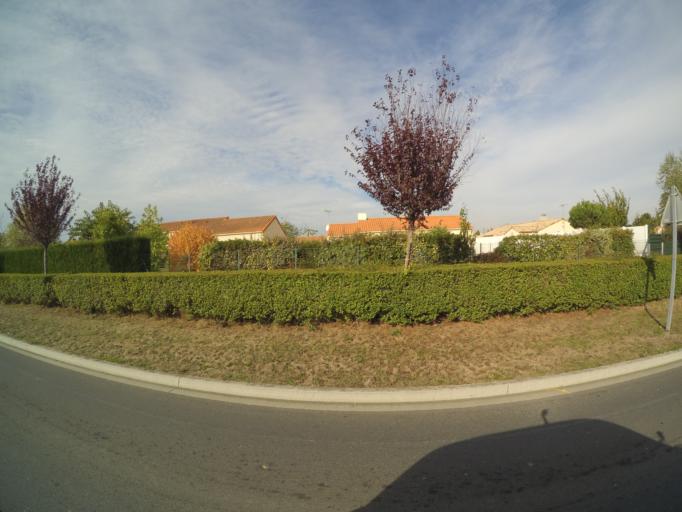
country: FR
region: Pays de la Loire
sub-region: Departement de Maine-et-Loire
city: Tillieres
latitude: 47.1419
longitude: -1.1647
